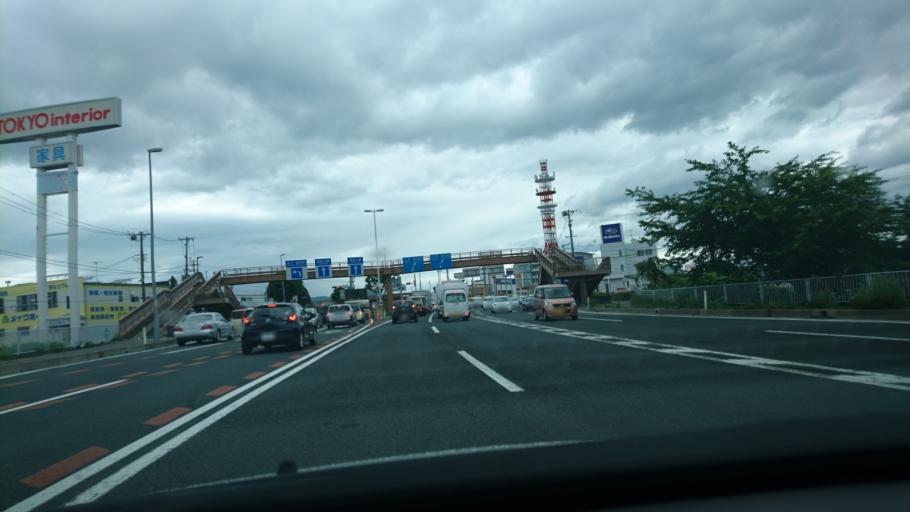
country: JP
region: Iwate
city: Morioka-shi
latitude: 39.7267
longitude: 141.1233
